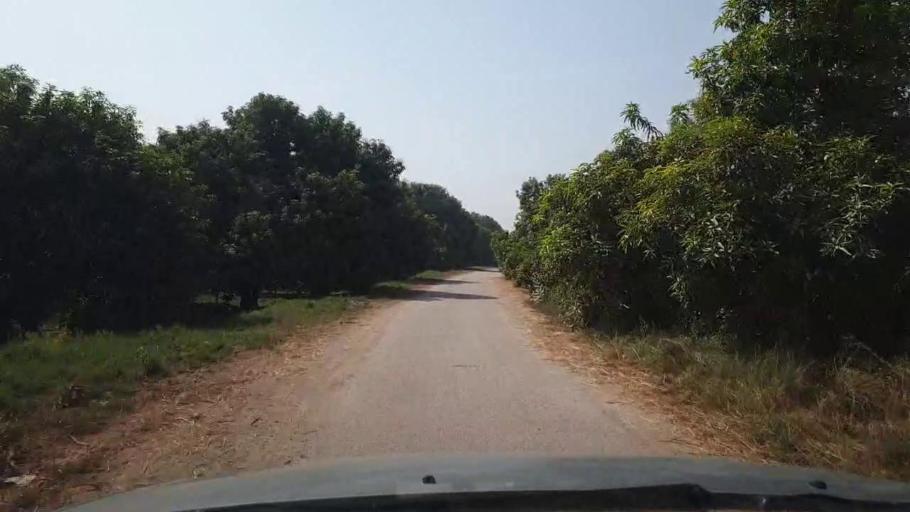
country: PK
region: Sindh
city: Tando Jam
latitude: 25.3624
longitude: 68.5243
